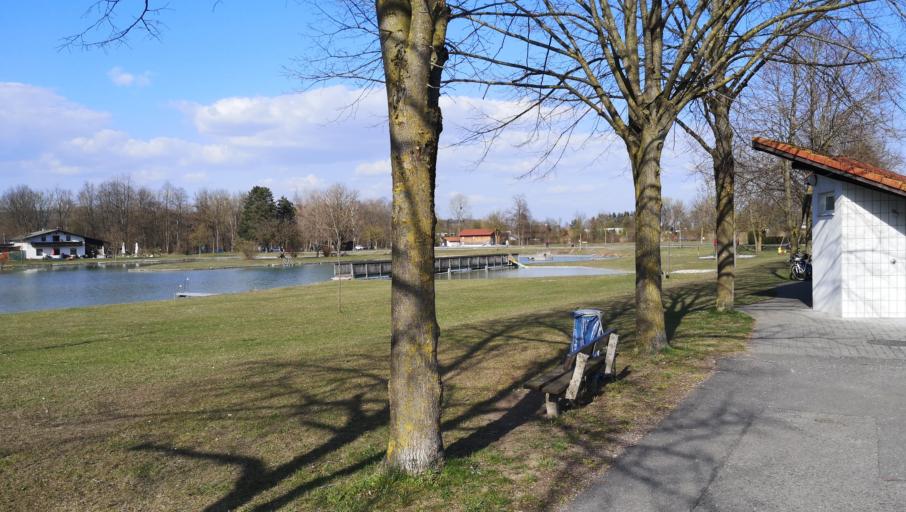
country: AT
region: Lower Austria
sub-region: Politischer Bezirk Melk
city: Blindenmarkt
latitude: 48.1161
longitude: 14.9882
